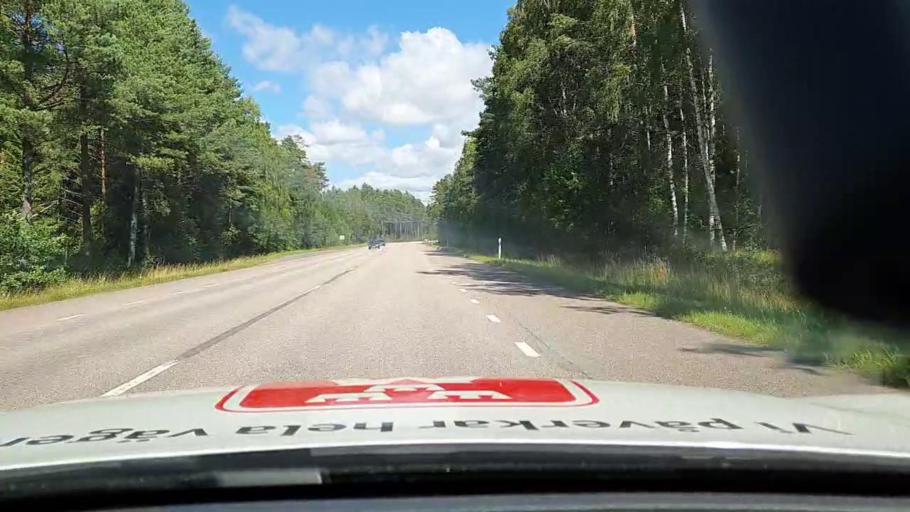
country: SE
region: Vaestra Goetaland
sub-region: Skovde Kommun
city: Stopen
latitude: 58.4289
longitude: 13.9136
